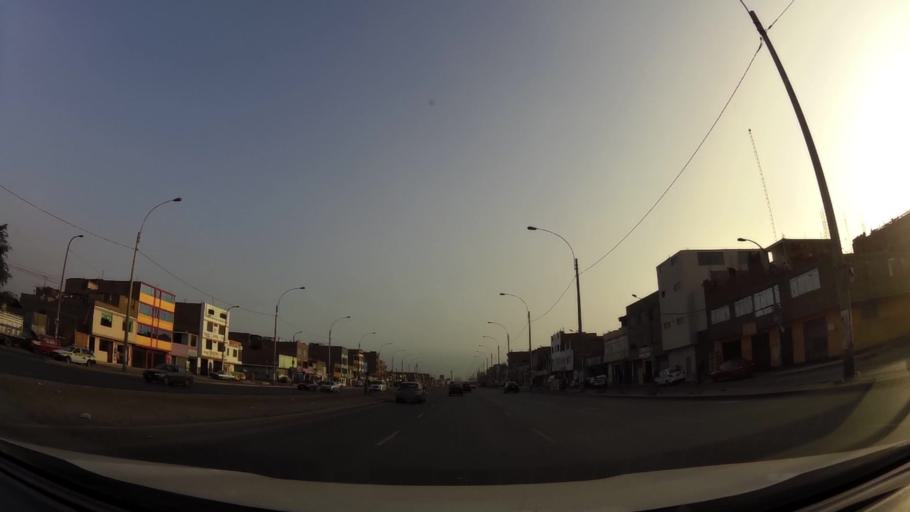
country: PE
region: Lima
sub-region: Lima
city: Independencia
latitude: -11.9920
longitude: -77.1083
